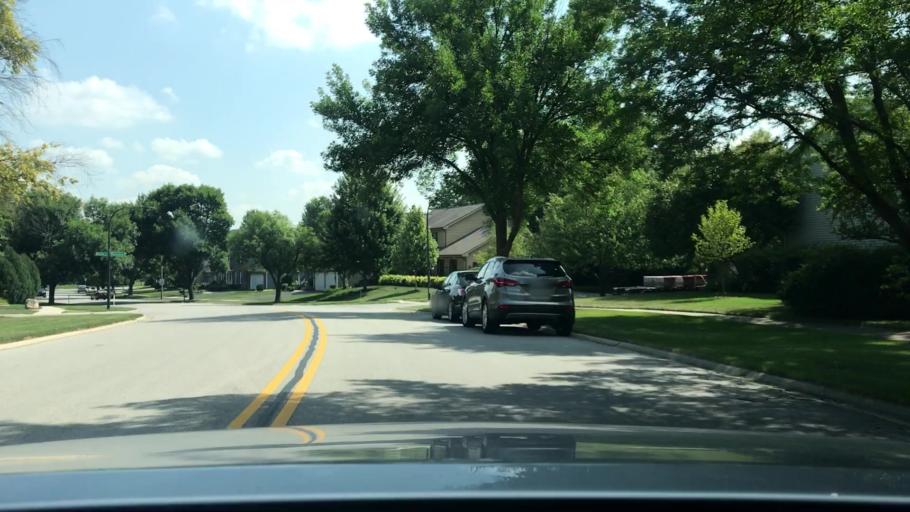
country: US
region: Illinois
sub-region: DuPage County
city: Naperville
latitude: 41.7408
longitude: -88.1445
